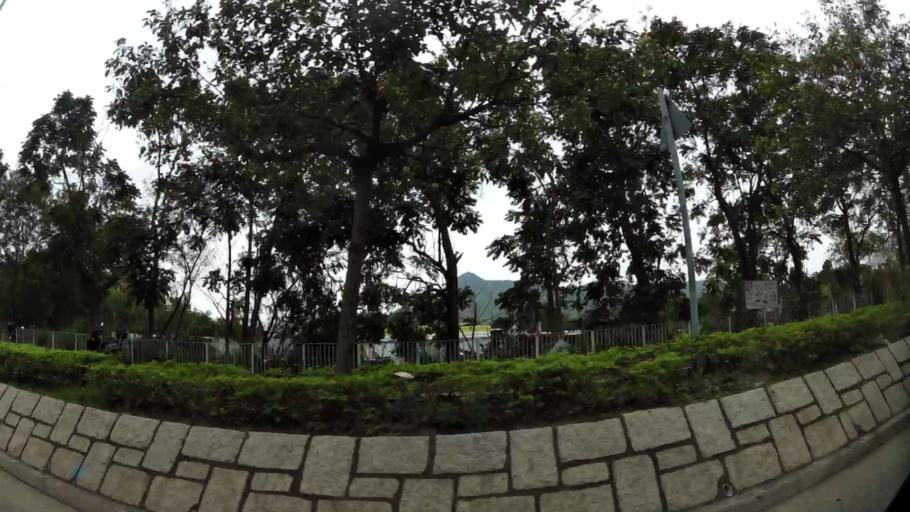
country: HK
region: Yuen Long
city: Yuen Long Kau Hui
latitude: 22.4377
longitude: 113.9964
